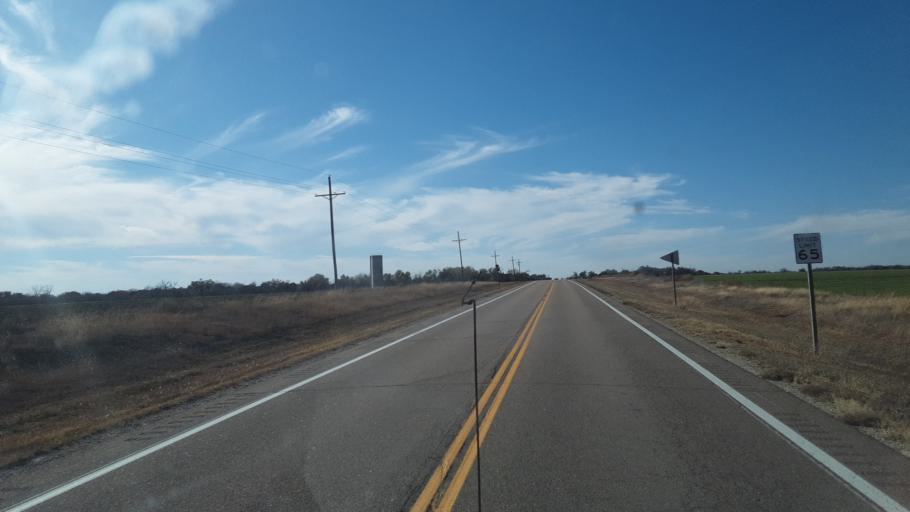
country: US
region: Kansas
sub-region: Pawnee County
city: Larned
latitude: 38.1896
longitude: -99.3167
